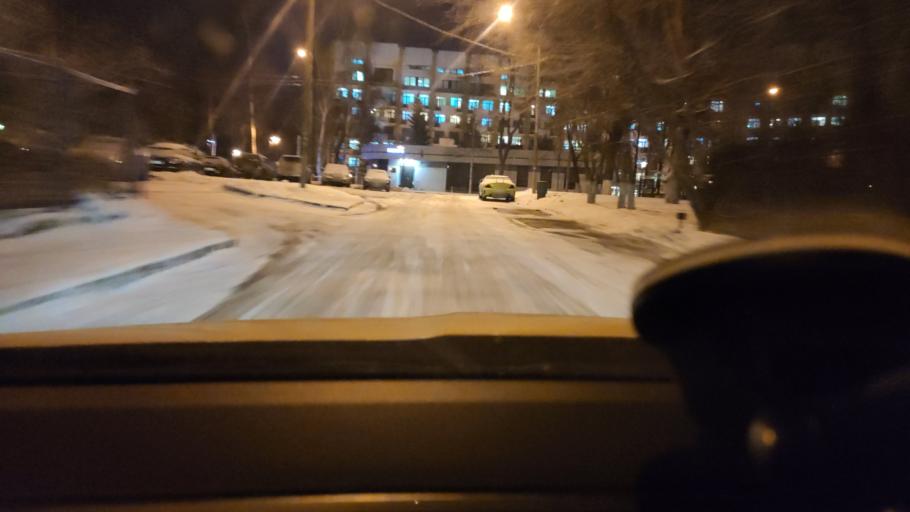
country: RU
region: Moskovskaya
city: Bogorodskoye
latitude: 55.8055
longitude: 37.6947
